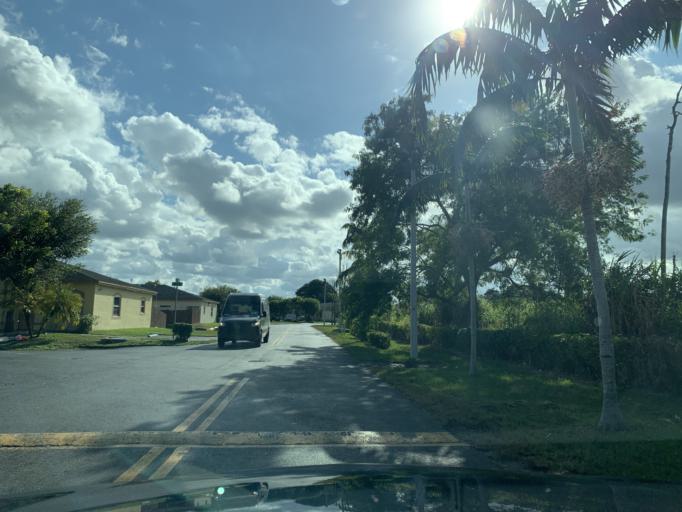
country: US
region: Florida
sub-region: Miami-Dade County
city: Naranja
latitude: 25.5050
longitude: -80.4182
